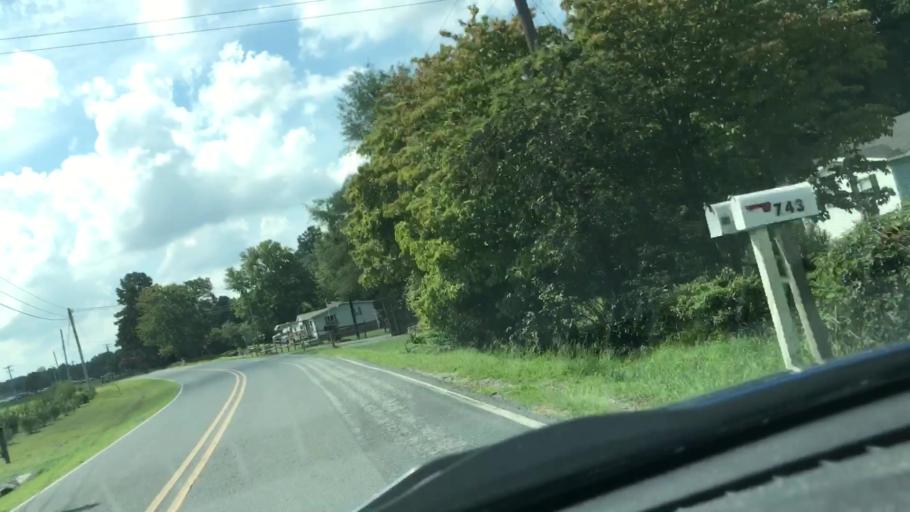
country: US
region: North Carolina
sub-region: Randolph County
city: Randleman
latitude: 35.8064
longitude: -79.8168
